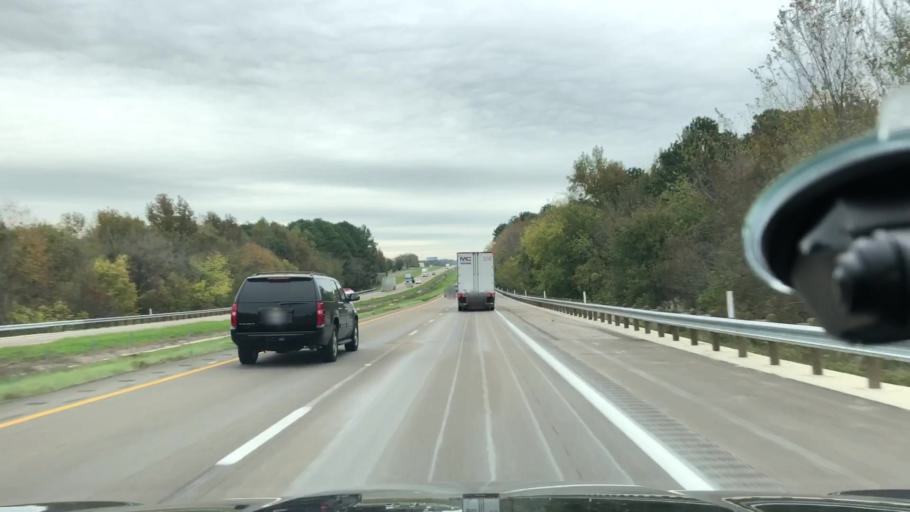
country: US
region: Texas
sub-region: Titus County
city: Mount Pleasant
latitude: 33.1595
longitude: -95.0322
